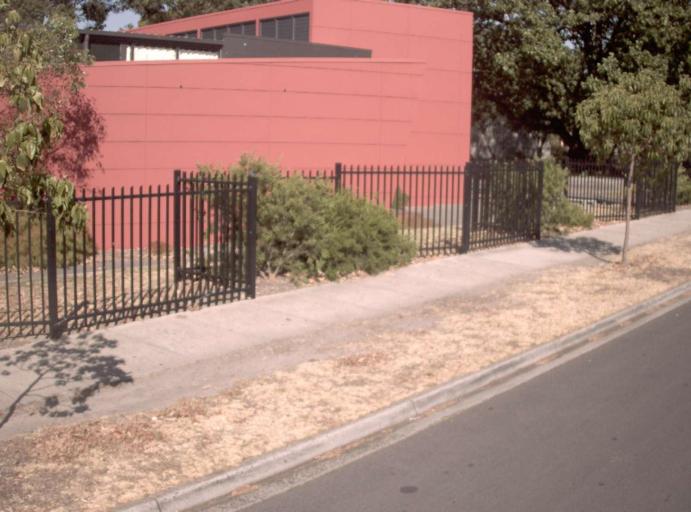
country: AU
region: Victoria
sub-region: Glen Eira
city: Glen Huntly
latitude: -37.8856
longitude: 145.0377
